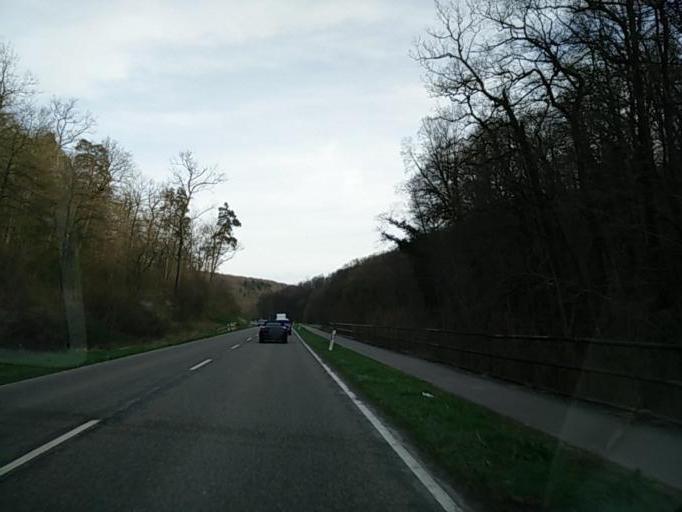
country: DE
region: Baden-Wuerttemberg
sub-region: Tuebingen Region
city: Tuebingen
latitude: 48.5530
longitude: 9.0693
